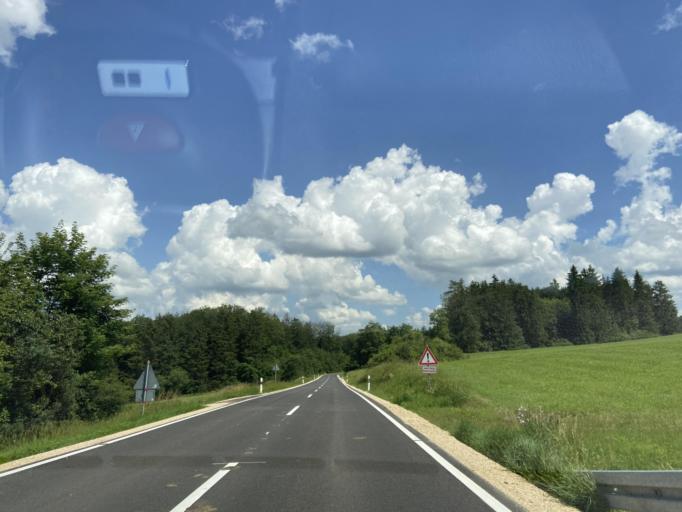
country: DE
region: Baden-Wuerttemberg
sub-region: Tuebingen Region
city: Veringenstadt
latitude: 48.1695
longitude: 9.1693
